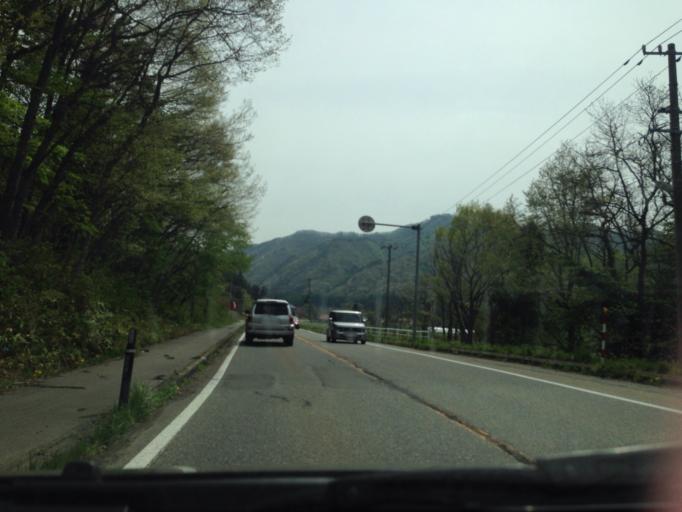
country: JP
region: Tochigi
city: Kuroiso
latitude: 37.1367
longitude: 139.7196
